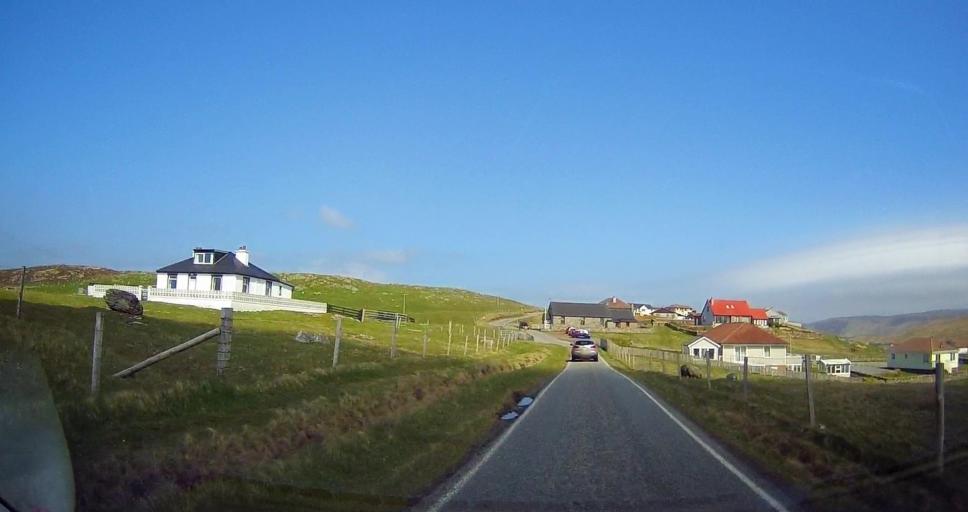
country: GB
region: Scotland
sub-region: Shetland Islands
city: Sandwick
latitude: 60.0850
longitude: -1.3317
